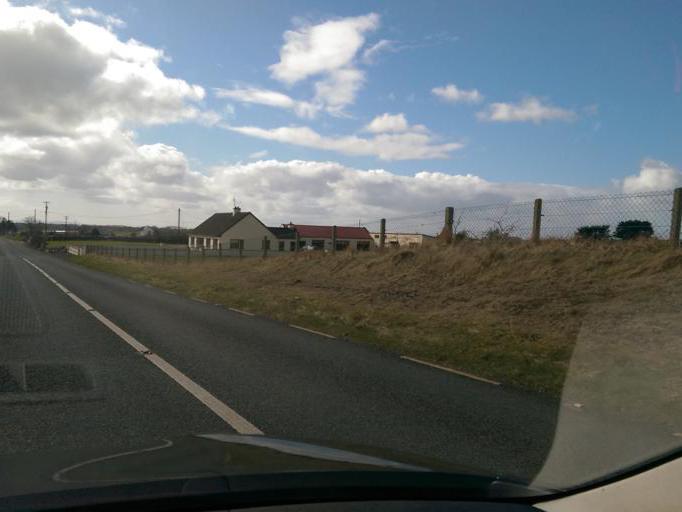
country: IE
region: Connaught
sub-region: County Galway
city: Athenry
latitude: 53.3605
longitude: -8.7315
